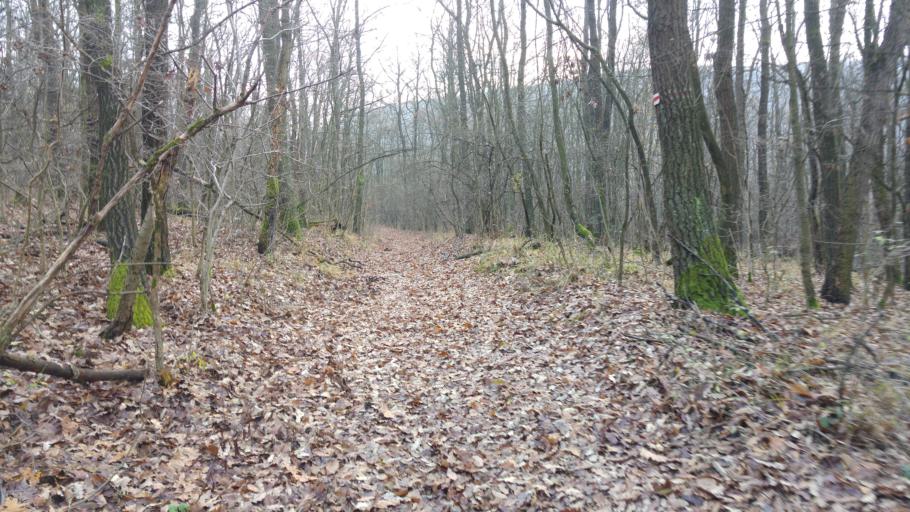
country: HU
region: Pest
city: Nagymaros
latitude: 47.8177
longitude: 18.9528
